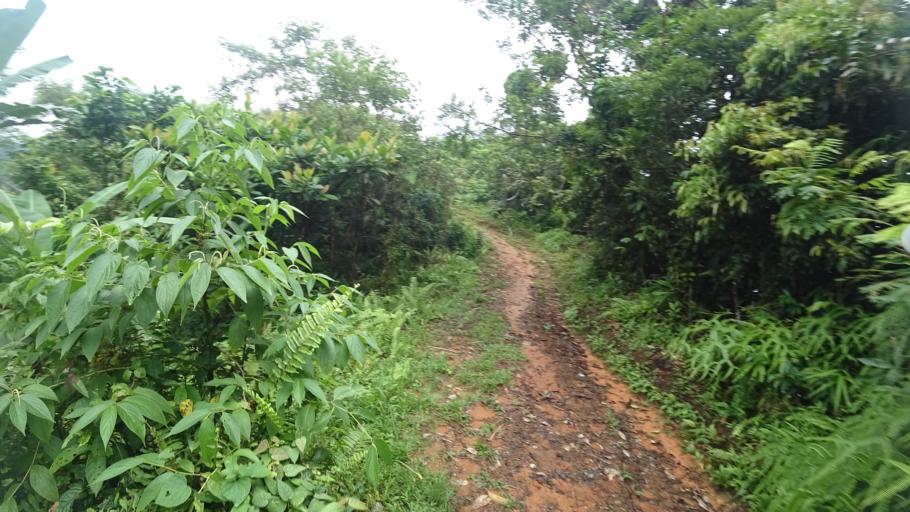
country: PH
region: Eastern Visayas
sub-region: Province of Leyte
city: Bugho
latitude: 10.8279
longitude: 124.8693
